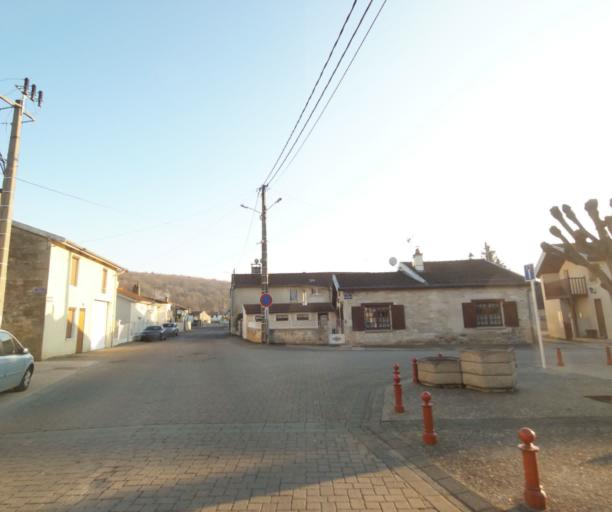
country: FR
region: Champagne-Ardenne
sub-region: Departement de la Haute-Marne
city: Chevillon
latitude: 48.5394
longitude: 5.1042
